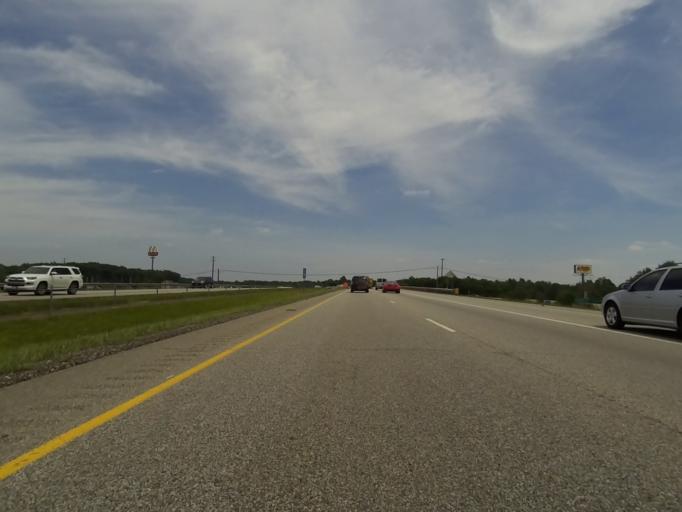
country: US
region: Ohio
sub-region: Portage County
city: Ravenna
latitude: 41.1096
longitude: -81.2446
